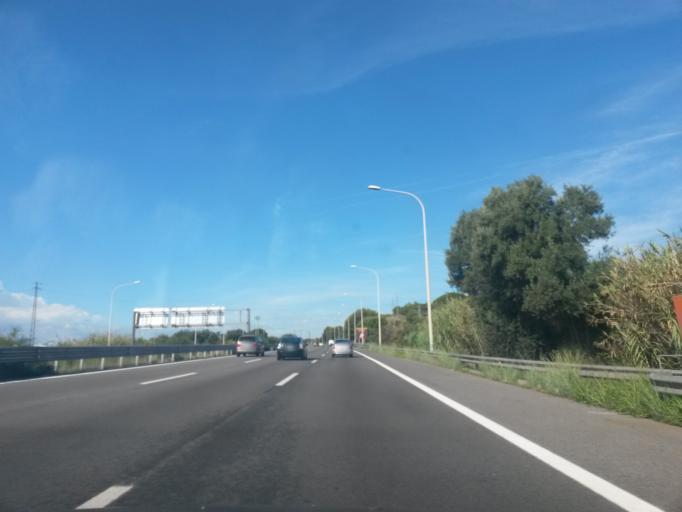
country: ES
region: Catalonia
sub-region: Provincia de Barcelona
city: Vilassar de Mar
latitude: 41.5168
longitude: 2.3886
